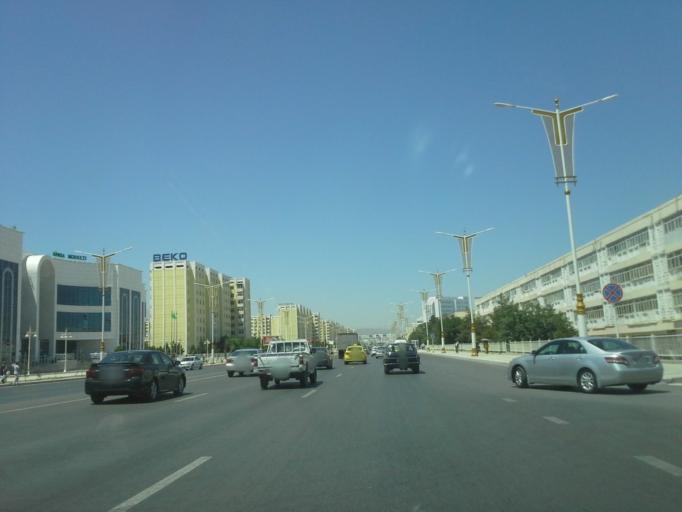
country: TM
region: Ahal
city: Ashgabat
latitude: 37.9103
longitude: 58.4052
